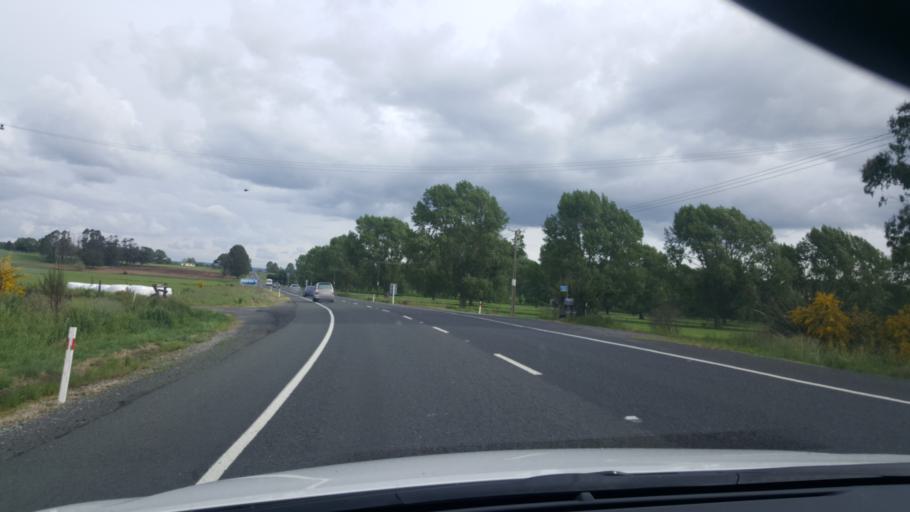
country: NZ
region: Waikato
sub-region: Taupo District
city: Taupo
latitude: -38.4875
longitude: 176.2905
